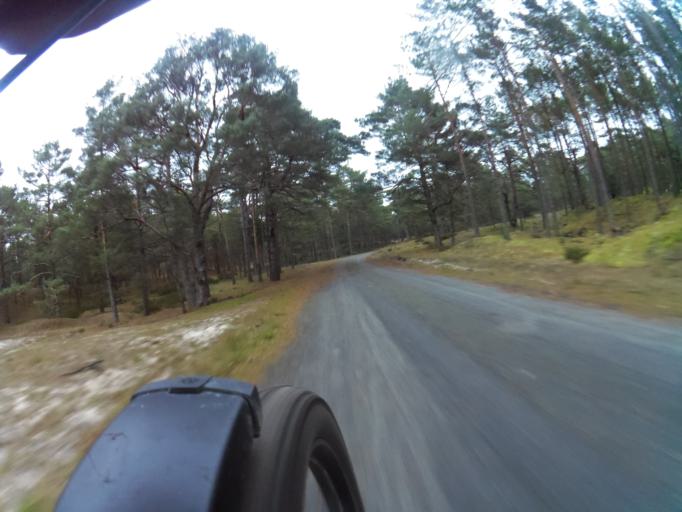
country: PL
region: Pomeranian Voivodeship
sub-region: Powiat wejherowski
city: Choczewo
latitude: 54.7901
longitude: 17.7559
